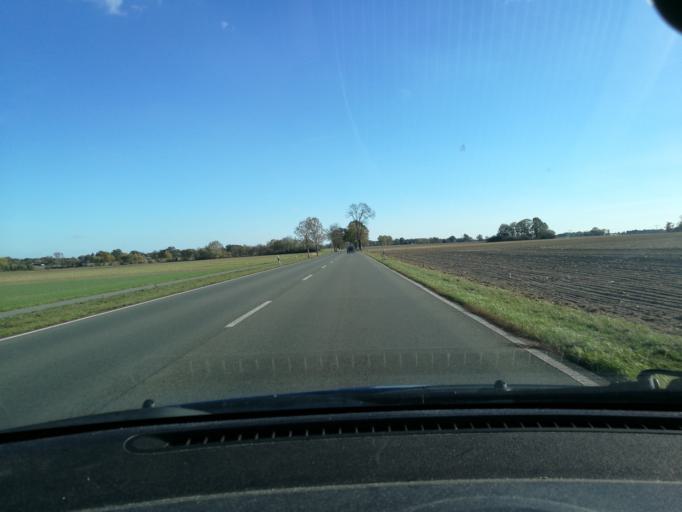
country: DE
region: Brandenburg
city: Karstadt
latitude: 53.1269
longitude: 11.7959
